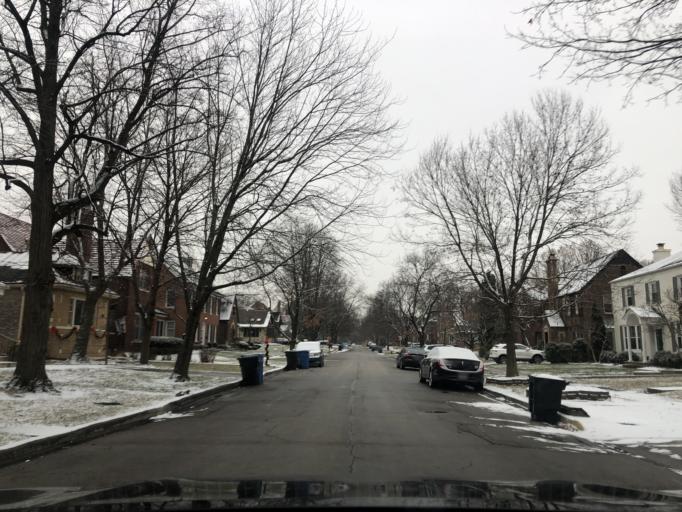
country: US
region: Illinois
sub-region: Cook County
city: Evergreen Park
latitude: 41.7310
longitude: -87.6776
